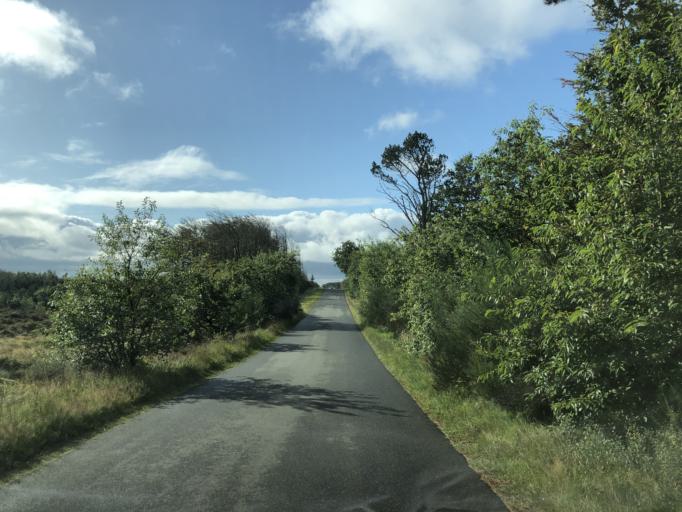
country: DK
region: Central Jutland
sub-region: Holstebro Kommune
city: Ulfborg
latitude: 56.3162
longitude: 8.4659
